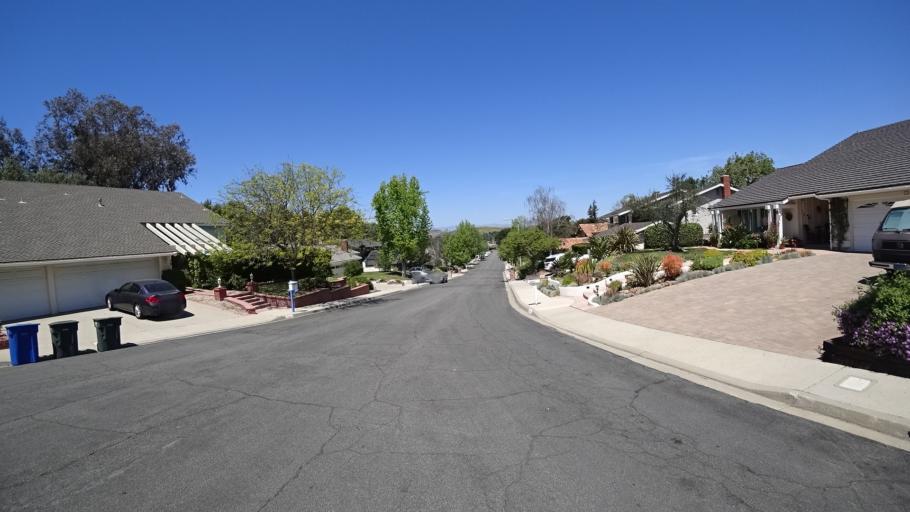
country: US
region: California
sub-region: Ventura County
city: Casa Conejo
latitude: 34.1784
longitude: -118.9030
